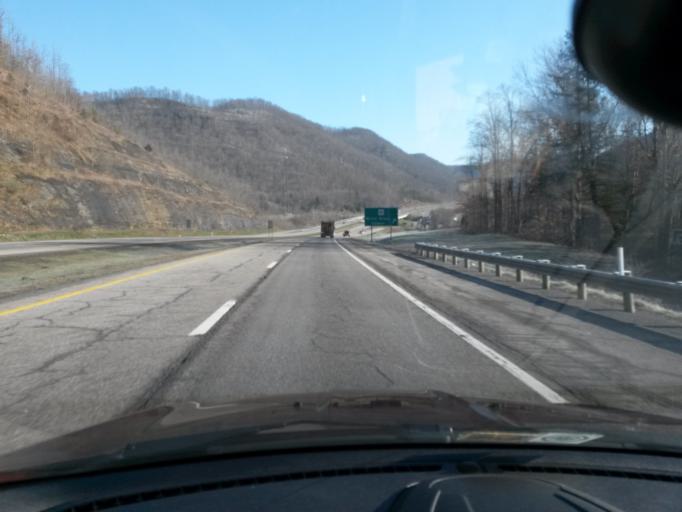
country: US
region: West Virginia
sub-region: Braxton County
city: Sutton
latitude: 38.4948
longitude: -80.7581
